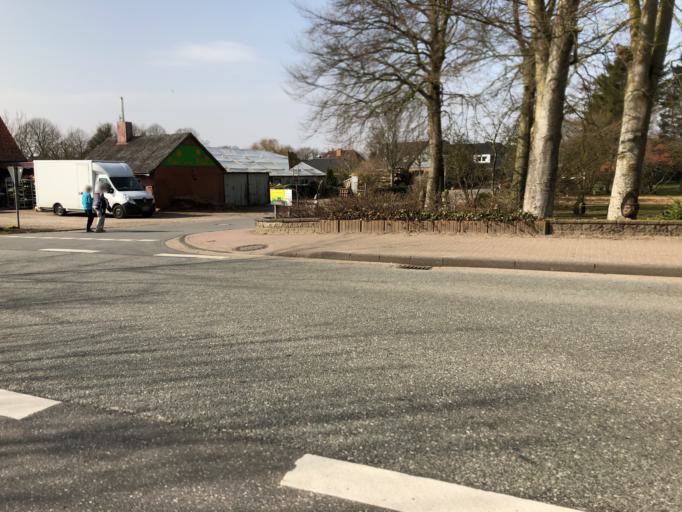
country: DE
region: Schleswig-Holstein
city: Wanderup
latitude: 54.6875
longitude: 9.3356
